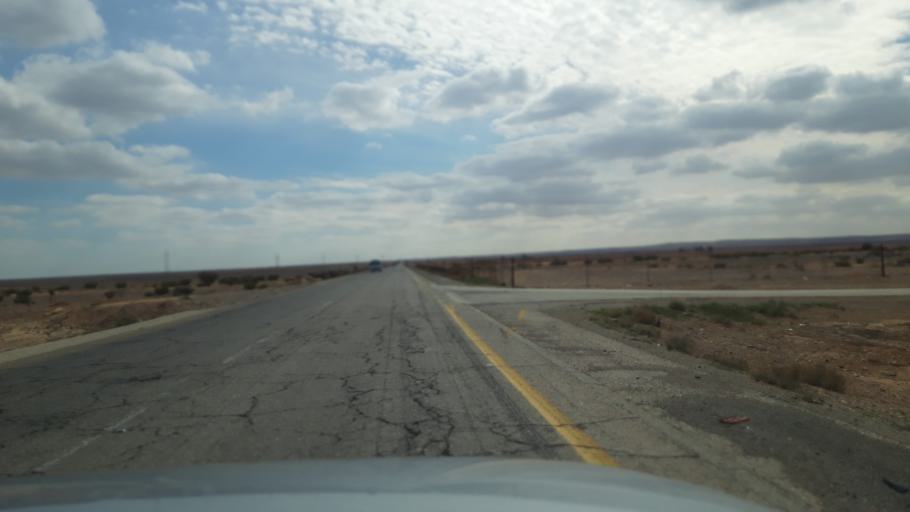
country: JO
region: Amman
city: Al Azraq ash Shamali
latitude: 31.8025
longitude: 36.5903
